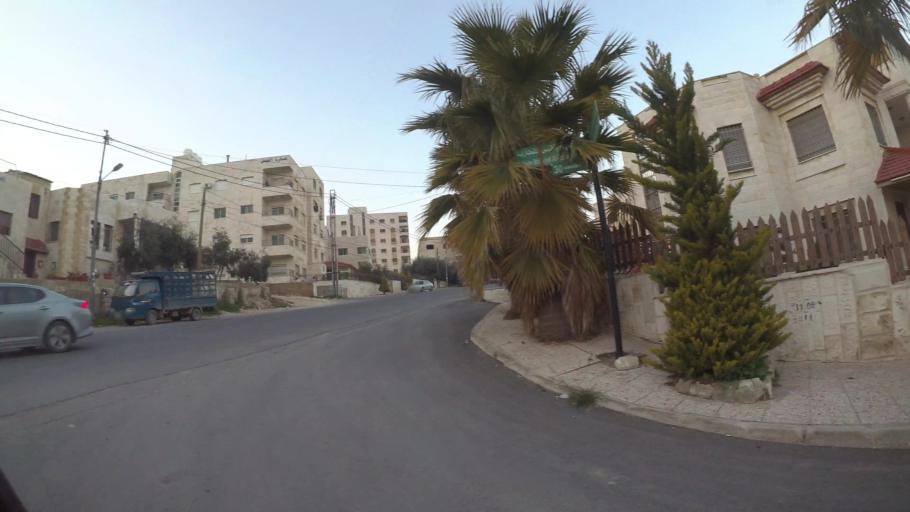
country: JO
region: Amman
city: Al Quwaysimah
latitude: 31.8948
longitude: 35.9291
